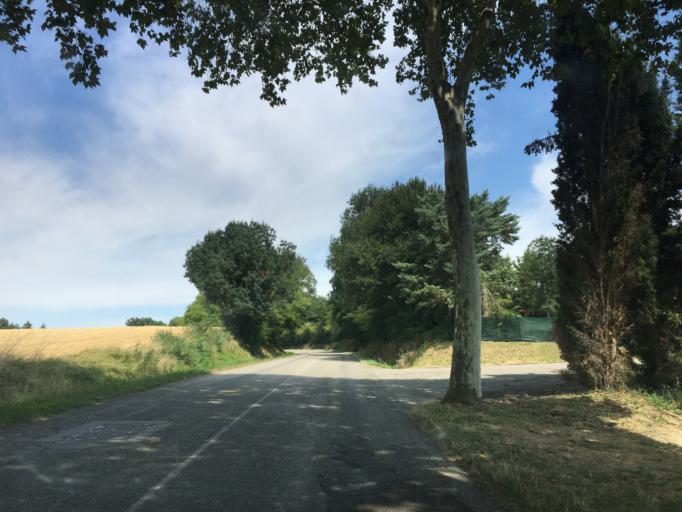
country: FR
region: Midi-Pyrenees
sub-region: Departement du Gers
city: Fleurance
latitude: 43.8559
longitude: 0.6789
